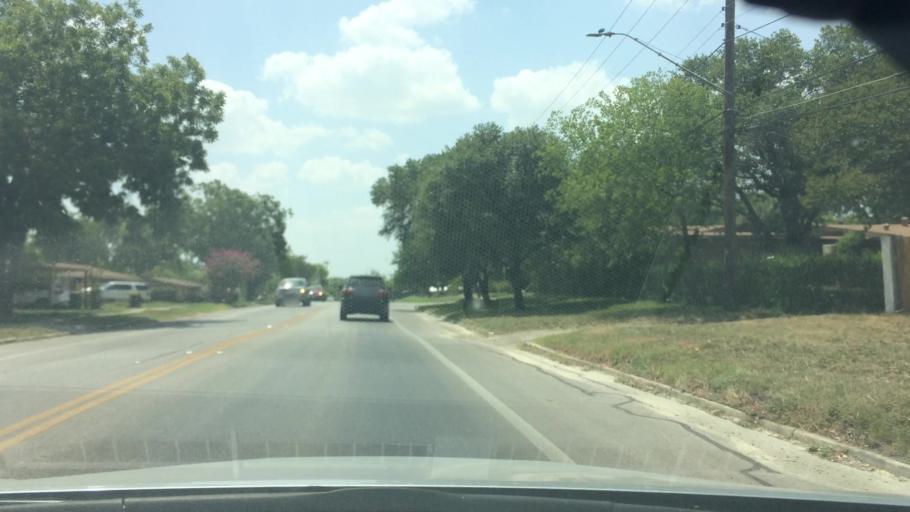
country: US
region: Texas
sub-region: Bexar County
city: Olmos Park
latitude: 29.5043
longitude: -98.4859
